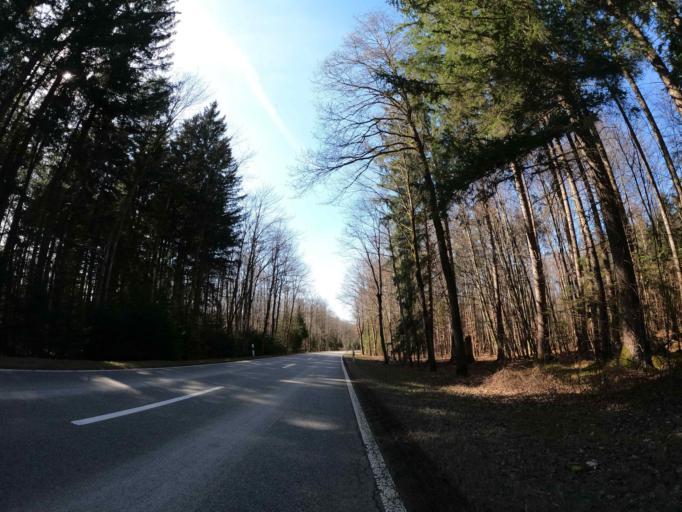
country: DE
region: Bavaria
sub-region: Upper Bavaria
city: Oberhaching
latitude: 48.0037
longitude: 11.6298
